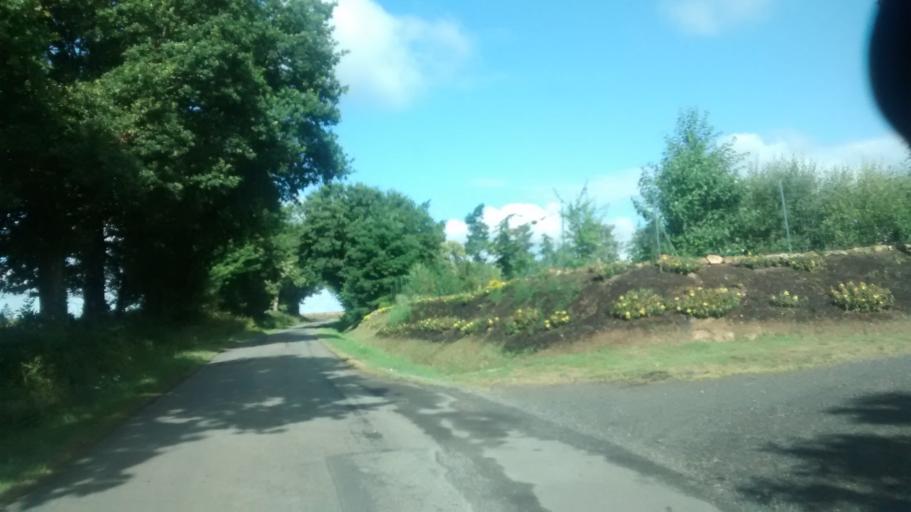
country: FR
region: Brittany
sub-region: Departement d'Ille-et-Vilaine
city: La Dominelais
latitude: 47.7842
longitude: -1.7061
